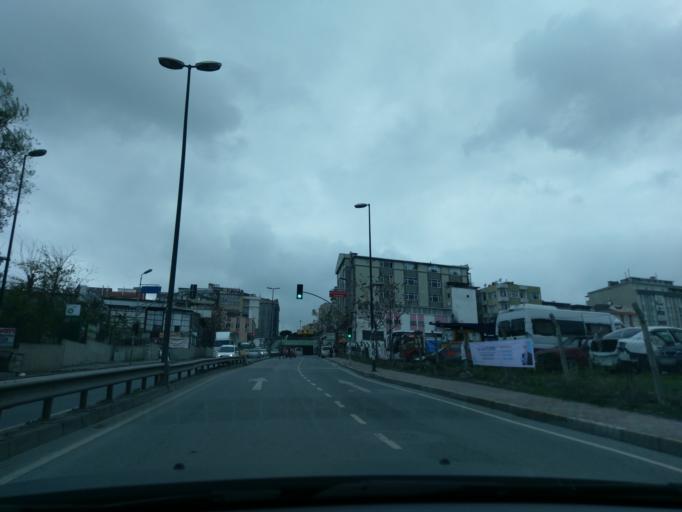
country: TR
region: Istanbul
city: Bahcelievler
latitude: 41.0135
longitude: 28.8457
